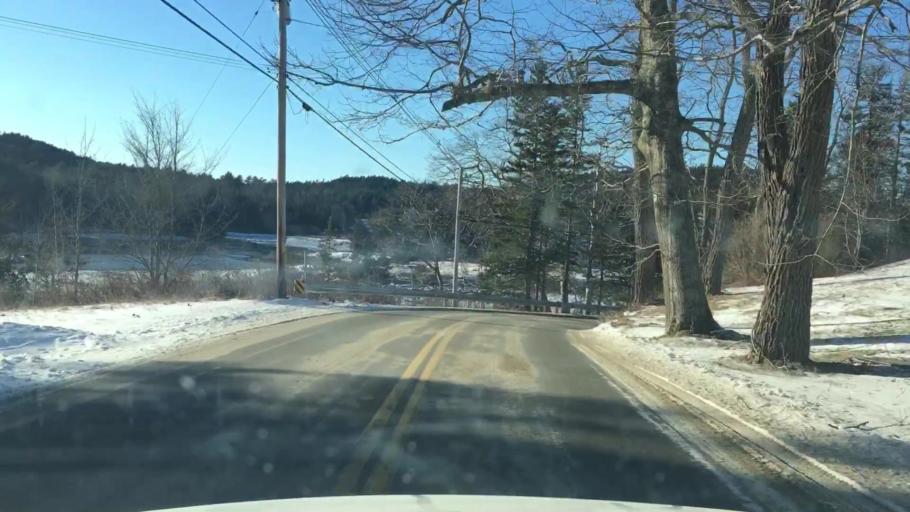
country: US
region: Maine
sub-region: Hancock County
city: Castine
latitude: 44.3491
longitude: -68.7482
